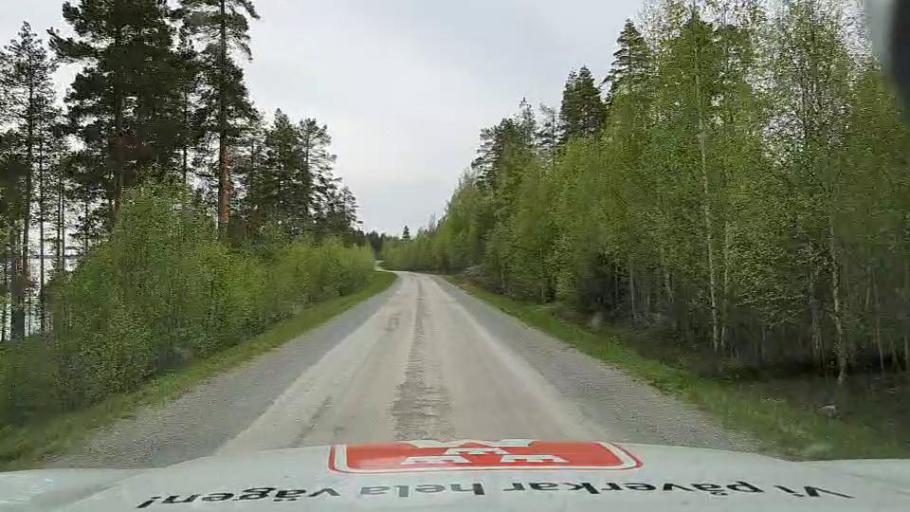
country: SE
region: Jaemtland
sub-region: Bergs Kommun
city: Hoverberg
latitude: 62.7326
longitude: 14.6648
